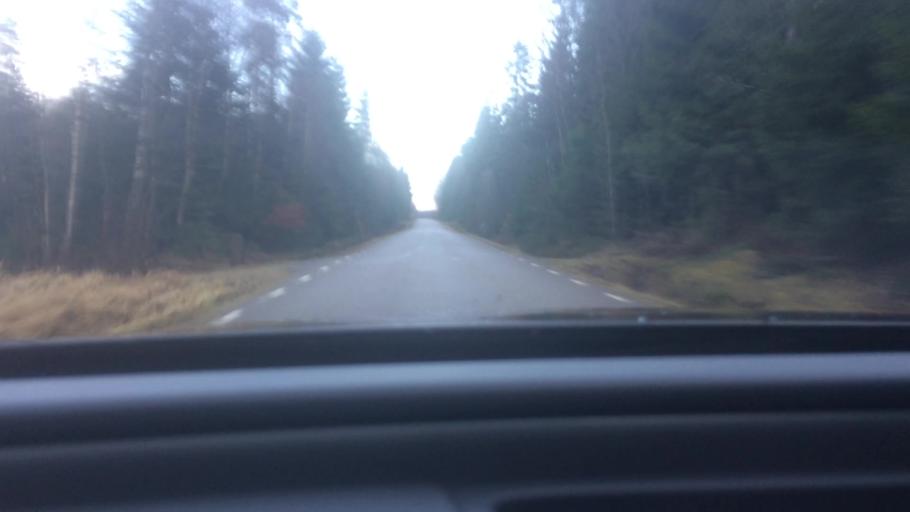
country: SE
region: Vaestra Goetaland
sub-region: Falkopings Kommun
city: Falkoeping
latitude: 58.0064
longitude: 13.4933
